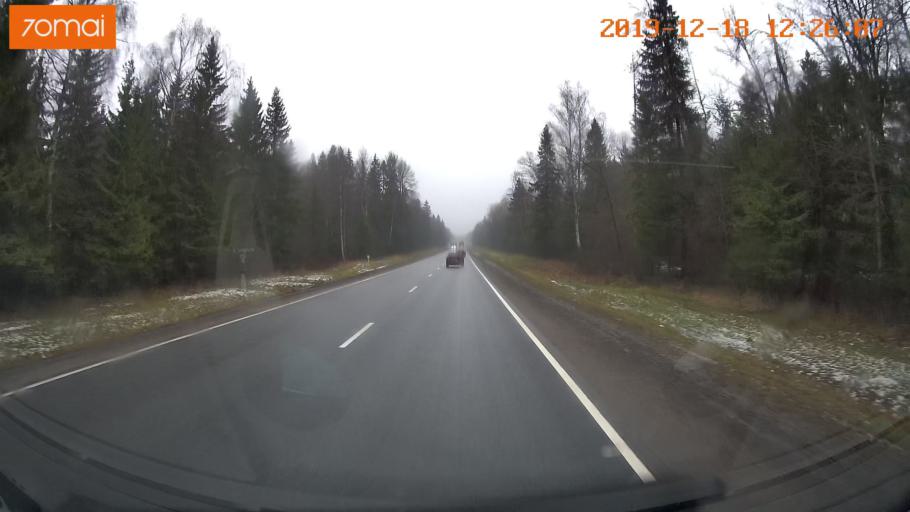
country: RU
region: Moskovskaya
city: Novopetrovskoye
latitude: 56.0474
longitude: 36.5001
